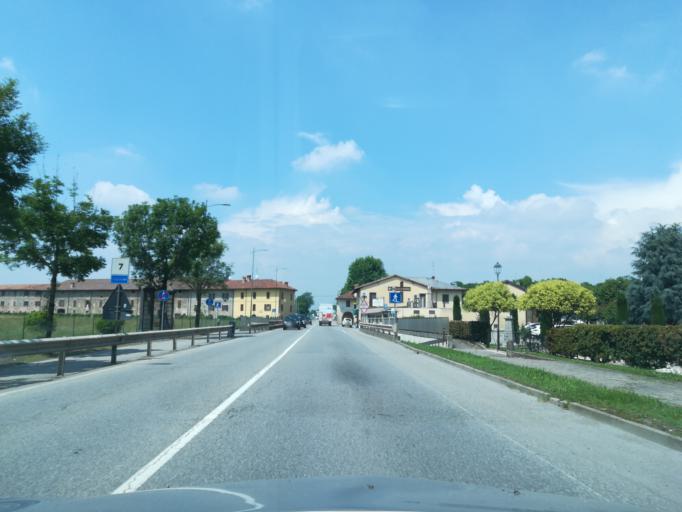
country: IT
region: Lombardy
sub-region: Provincia di Bergamo
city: Cavernago
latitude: 45.6297
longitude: 9.7656
